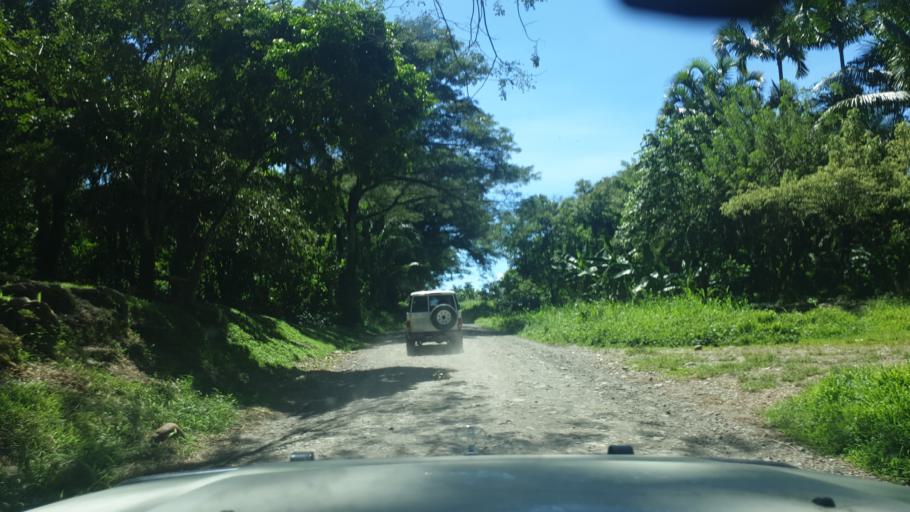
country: PG
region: Bougainville
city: Arawa
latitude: -5.8136
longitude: 155.1486
